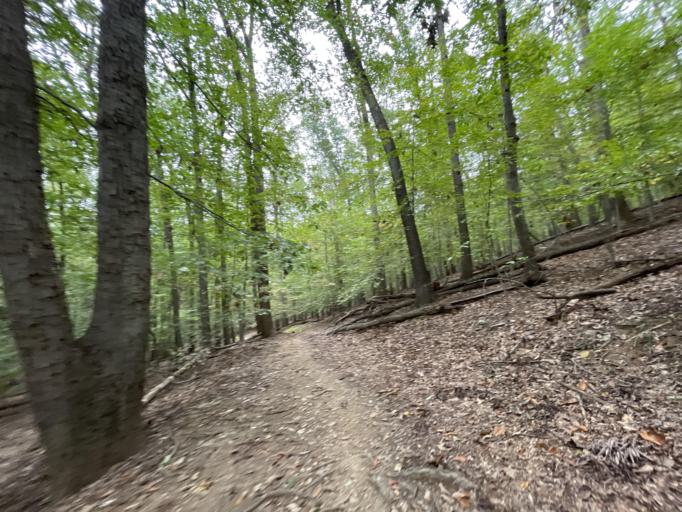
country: US
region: Maryland
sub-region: Baltimore County
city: Hampton
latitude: 39.4299
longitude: -76.5701
